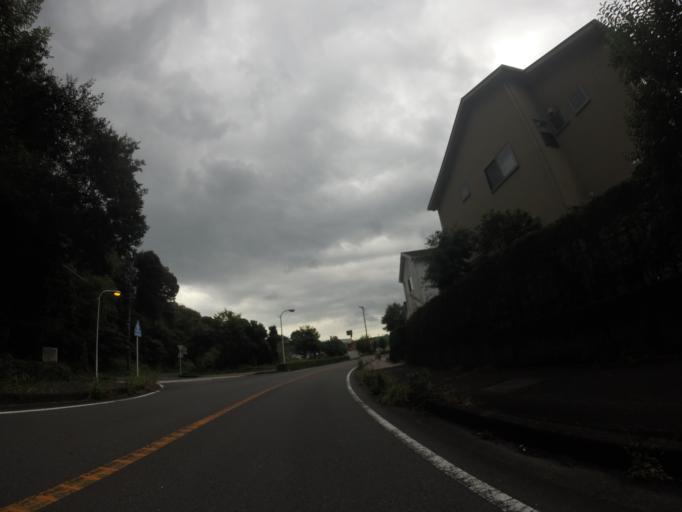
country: JP
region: Shizuoka
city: Fujieda
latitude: 34.8942
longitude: 138.2643
